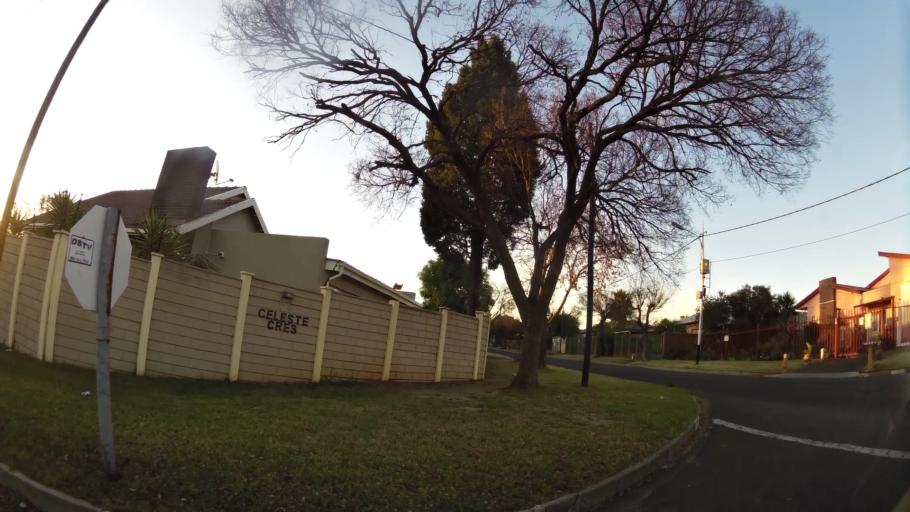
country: ZA
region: Gauteng
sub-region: City of Johannesburg Metropolitan Municipality
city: Roodepoort
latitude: -26.1572
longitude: 27.8884
